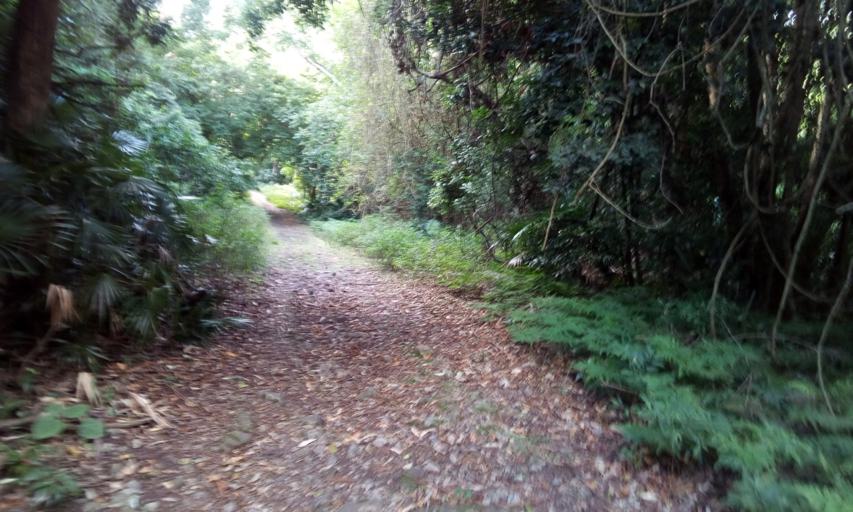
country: AU
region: New South Wales
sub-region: Wollongong
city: Cordeaux Heights
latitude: -34.4430
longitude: 150.8112
